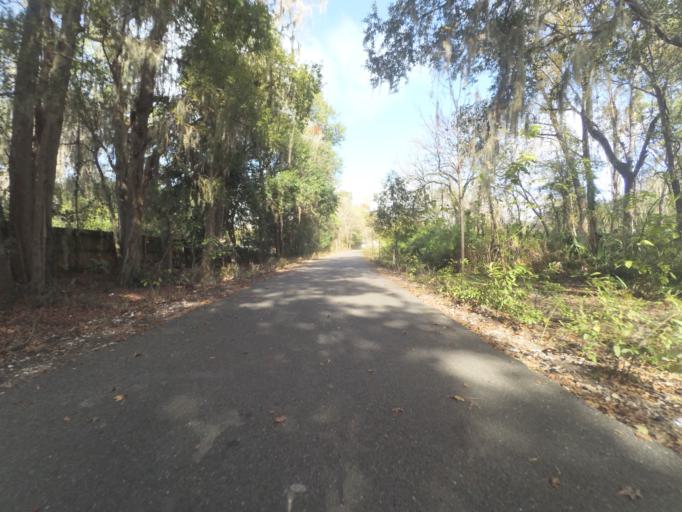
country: US
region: Florida
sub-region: Alachua County
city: Gainesville
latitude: 29.6652
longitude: -82.3262
